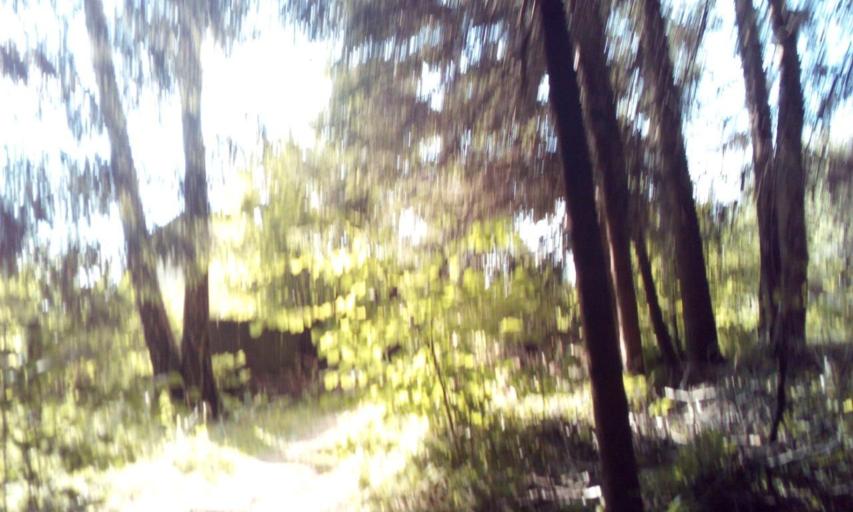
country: RU
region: Moskovskaya
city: Kievskij
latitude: 55.3423
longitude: 36.9653
